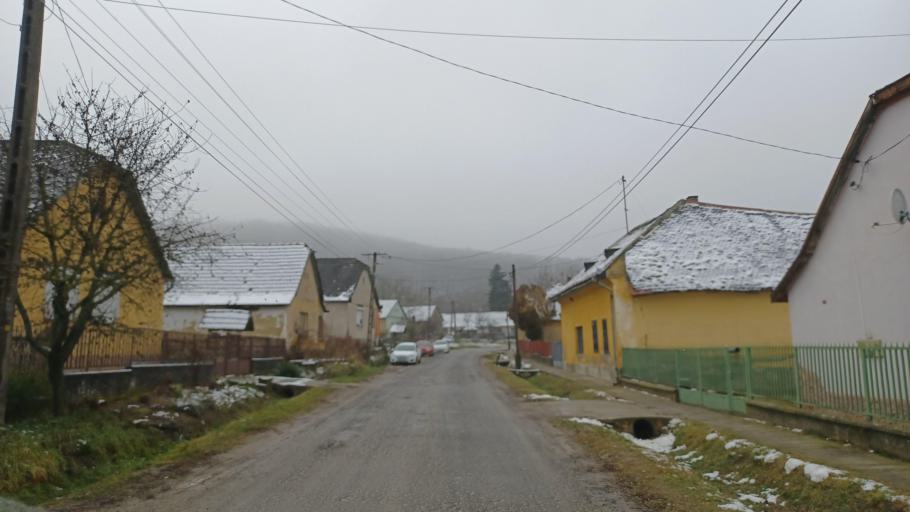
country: HU
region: Tolna
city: Pincehely
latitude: 46.6311
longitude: 18.4845
